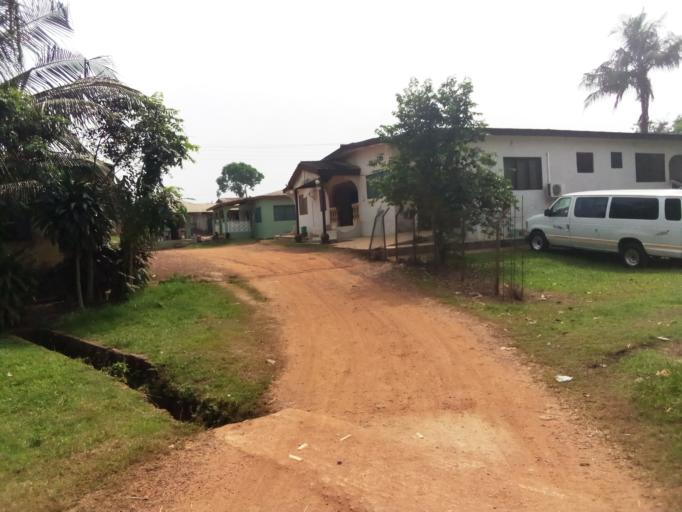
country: CI
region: Sud-Comoe
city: Ayame
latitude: 5.8274
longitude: -2.8190
